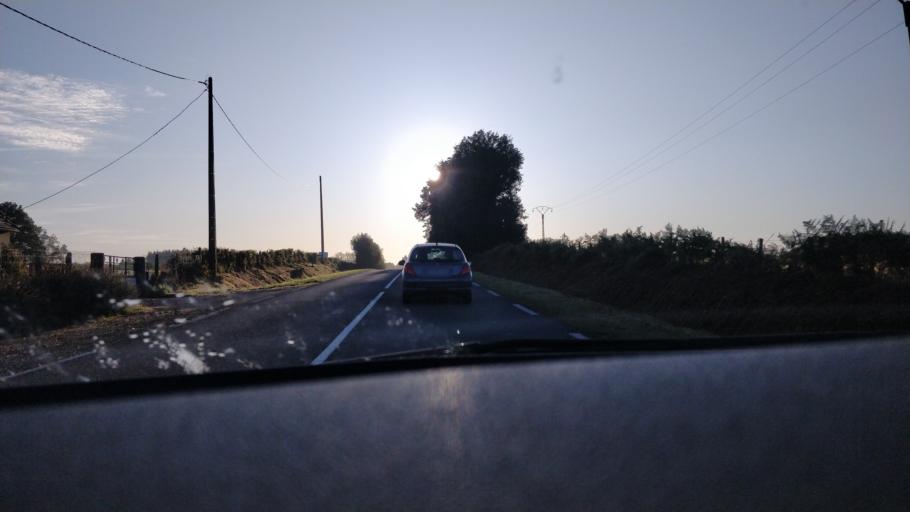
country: FR
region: Limousin
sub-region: Departement de la Creuse
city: Bourganeuf
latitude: 45.9495
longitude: 1.6906
